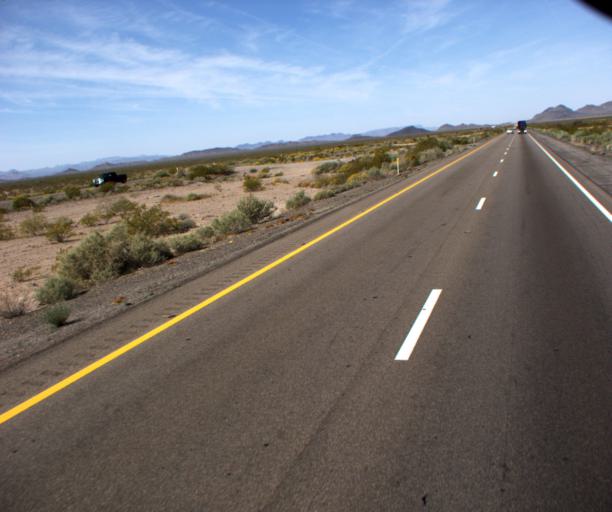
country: US
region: Arizona
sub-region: La Paz County
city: Salome
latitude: 33.5971
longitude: -113.5379
